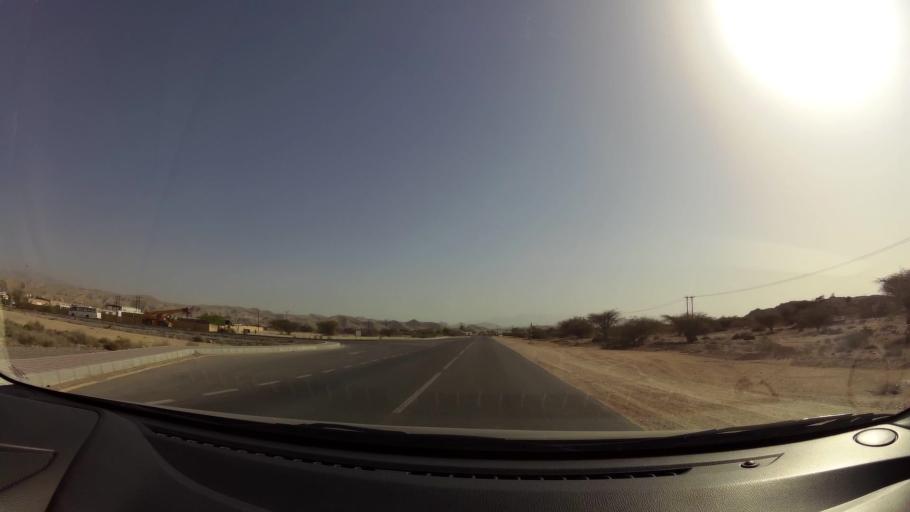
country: OM
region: Muhafazat Masqat
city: As Sib al Jadidah
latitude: 23.5825
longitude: 58.2405
